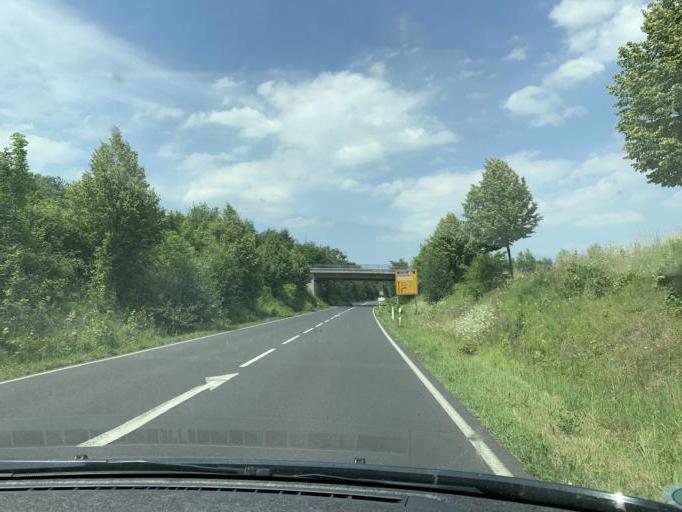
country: DE
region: North Rhine-Westphalia
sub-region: Regierungsbezirk Koln
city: Bedburg
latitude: 50.9979
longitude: 6.5863
